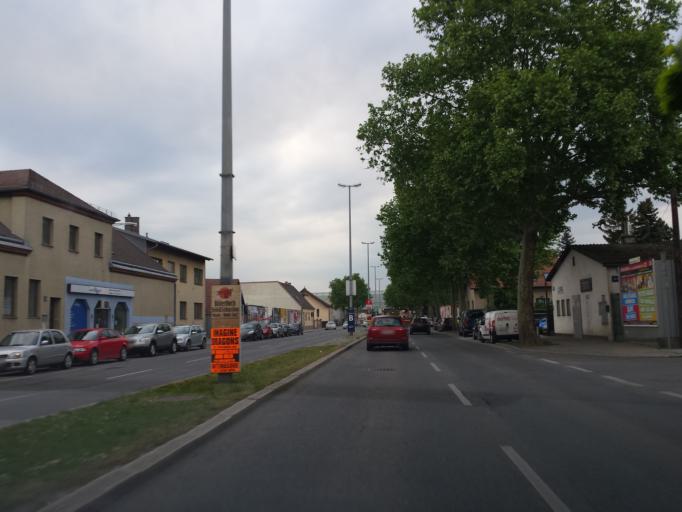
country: AT
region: Lower Austria
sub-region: Politischer Bezirk Wien-Umgebung
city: Gerasdorf bei Wien
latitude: 48.2212
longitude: 16.4775
